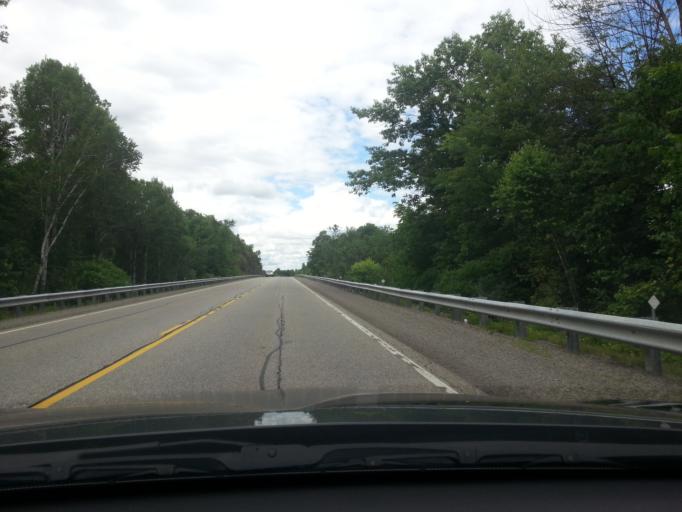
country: CA
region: Ontario
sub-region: Lanark County
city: Smiths Falls
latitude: 44.7824
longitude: -76.1072
